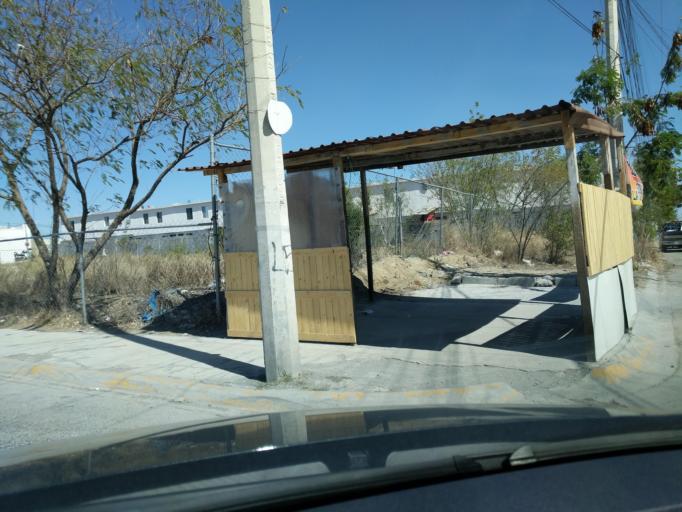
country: MX
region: Nuevo Leon
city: Juarez
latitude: 25.6348
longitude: -100.0877
